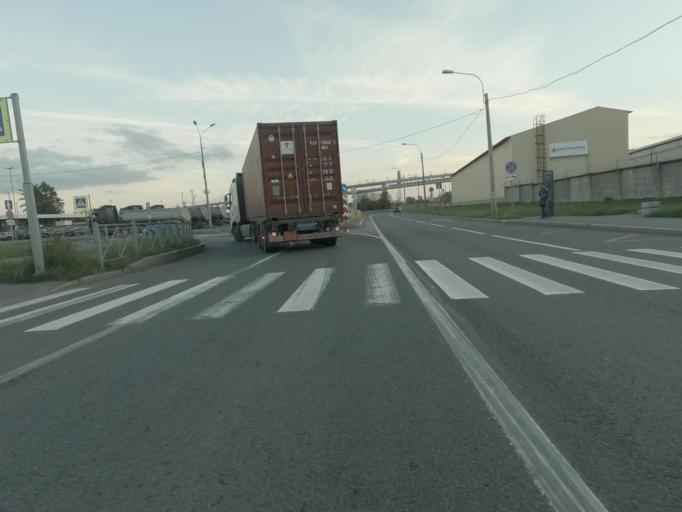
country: RU
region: St.-Petersburg
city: Vasyl'evsky Ostrov
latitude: 59.9046
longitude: 30.2348
